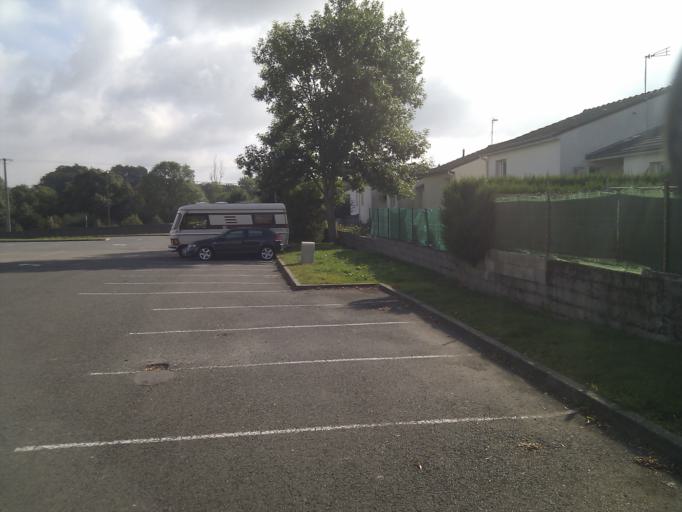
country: FR
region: Champagne-Ardenne
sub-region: Departement de la Haute-Marne
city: Chateauvillain
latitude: 48.0313
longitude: 4.9133
